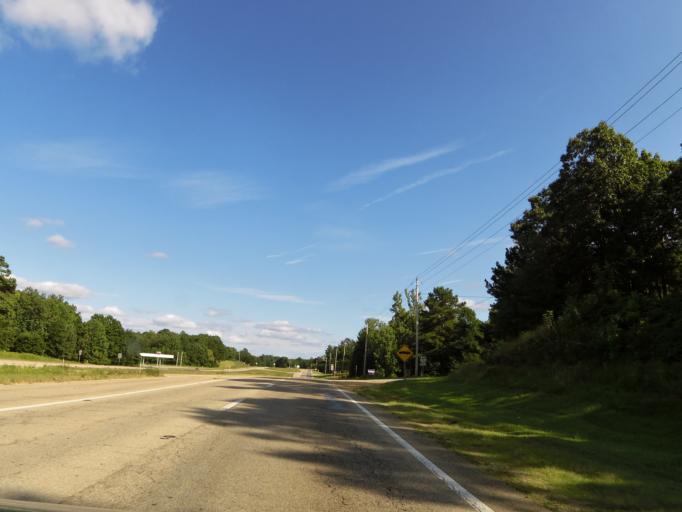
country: US
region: Mississippi
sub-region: Alcorn County
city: Farmington
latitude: 34.8668
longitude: -88.4207
